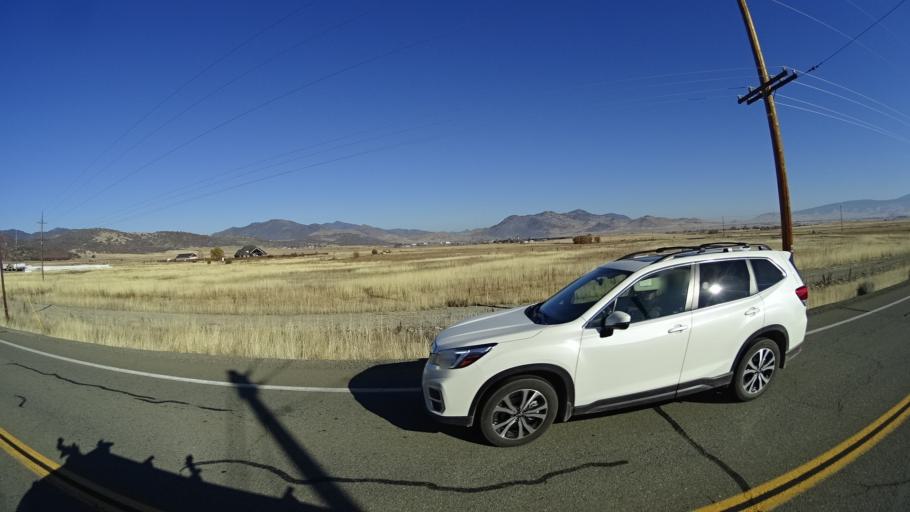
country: US
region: California
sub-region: Siskiyou County
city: Yreka
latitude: 41.7114
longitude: -122.5952
